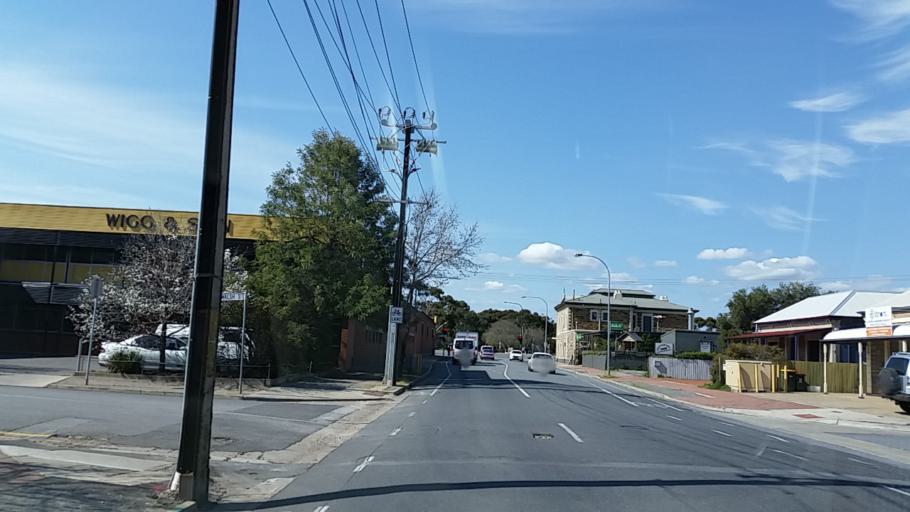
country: AU
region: South Australia
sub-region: City of West Torrens
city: Thebarton
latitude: -34.9136
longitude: 138.5763
